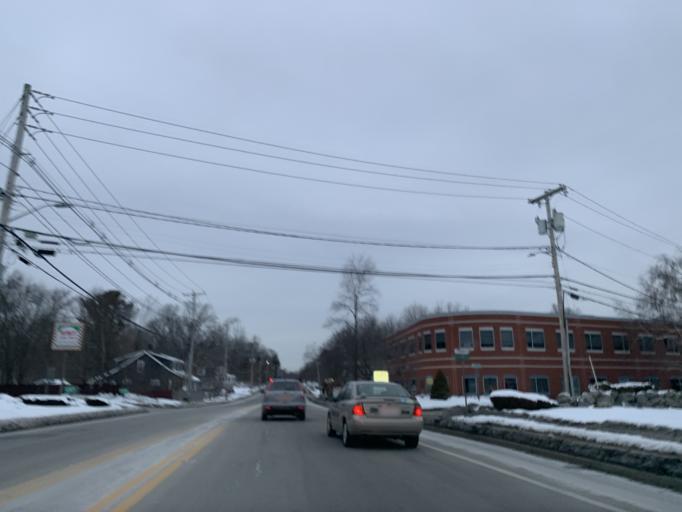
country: US
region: Massachusetts
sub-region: Norfolk County
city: Avon
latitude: 42.1033
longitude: -71.0681
